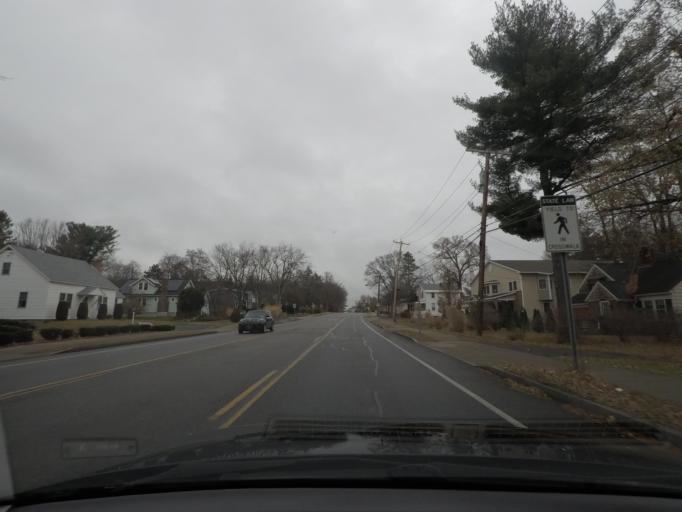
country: US
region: New York
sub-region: Albany County
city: McKownville
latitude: 42.6850
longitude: -73.8357
